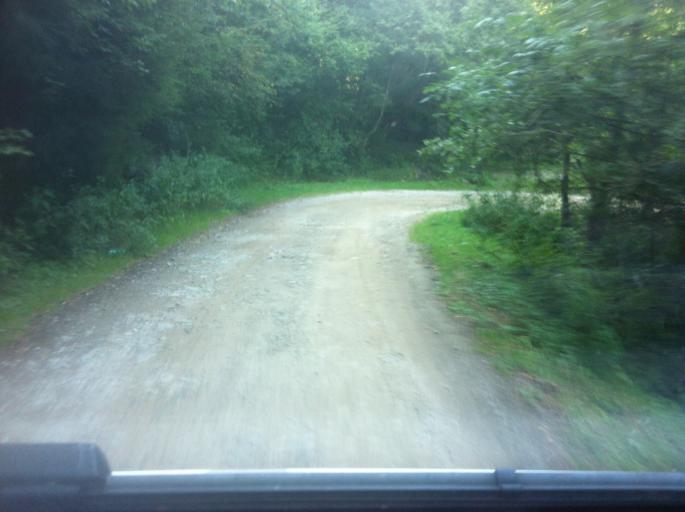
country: RO
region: Hunedoara
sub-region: Comuna Rau de Mori
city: Rau de Mori
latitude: 45.4404
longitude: 22.8919
